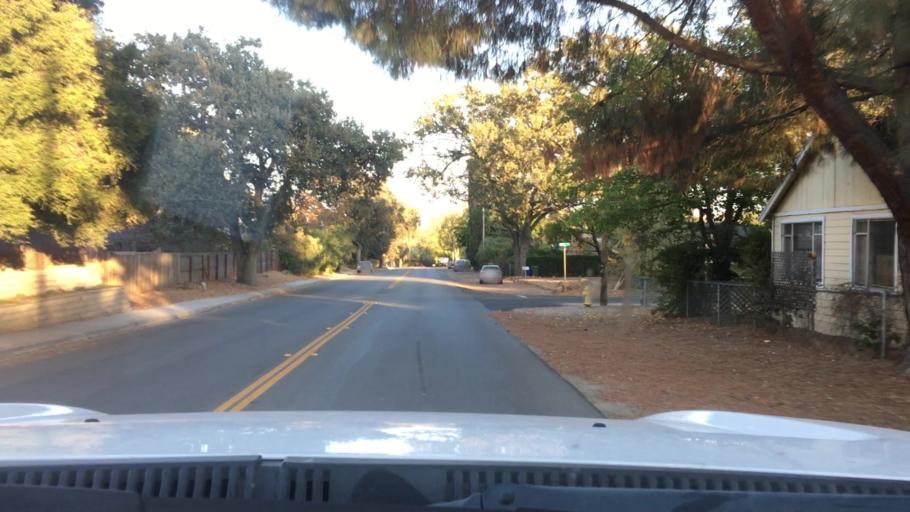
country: US
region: California
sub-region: San Luis Obispo County
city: Templeton
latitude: 35.5544
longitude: -120.7078
